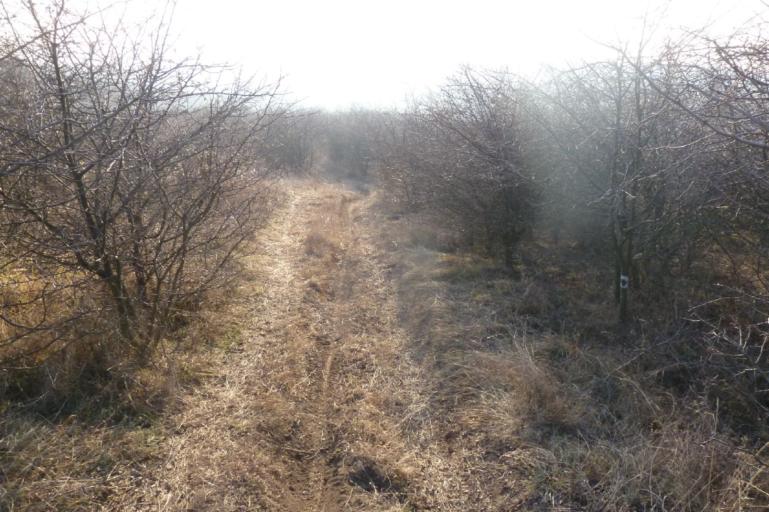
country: HU
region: Pest
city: Pecel
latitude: 47.5162
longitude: 19.3387
